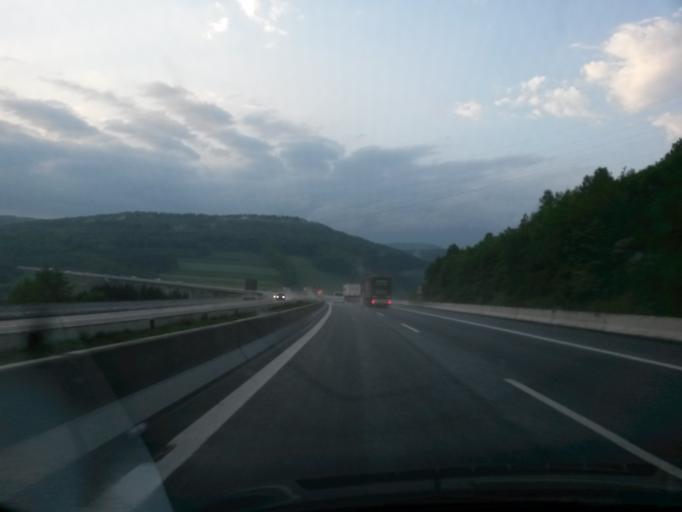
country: DE
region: Bavaria
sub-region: Regierungsbezirk Unterfranken
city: Riedenberg
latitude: 50.3110
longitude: 9.8481
